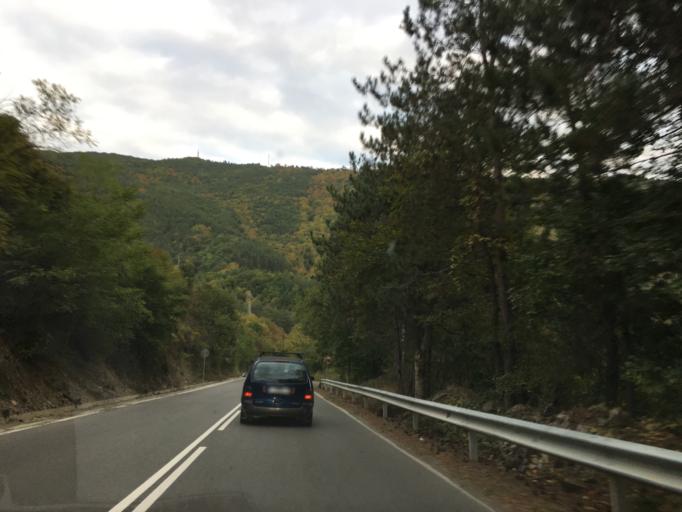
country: BG
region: Sofiya
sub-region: Obshtina Svoge
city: Svoge
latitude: 42.9455
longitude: 23.3811
